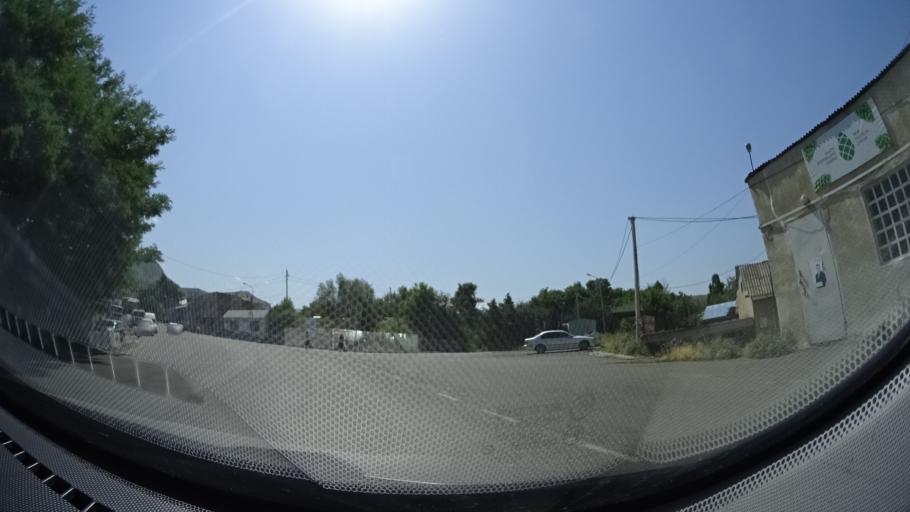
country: GE
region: Samtskhe-Javakheti
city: Aspindza
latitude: 41.5735
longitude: 43.2482
